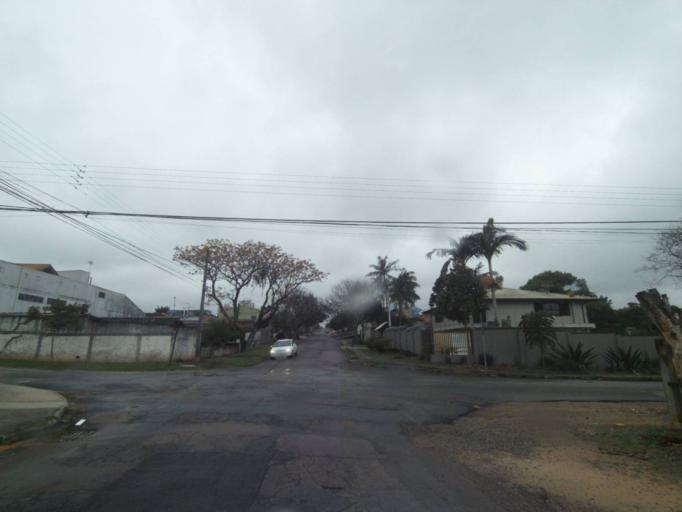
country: BR
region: Parana
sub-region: Curitiba
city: Curitiba
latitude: -25.5145
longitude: -49.3028
